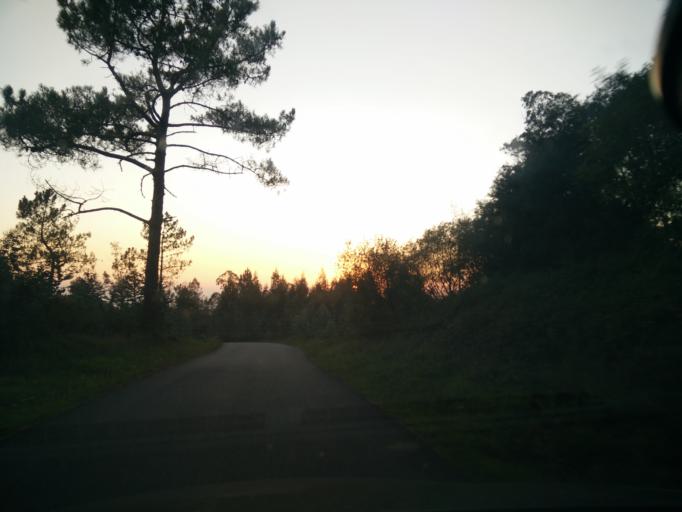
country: ES
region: Galicia
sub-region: Provincia da Coruna
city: Monfero
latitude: 43.3546
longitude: -8.0501
